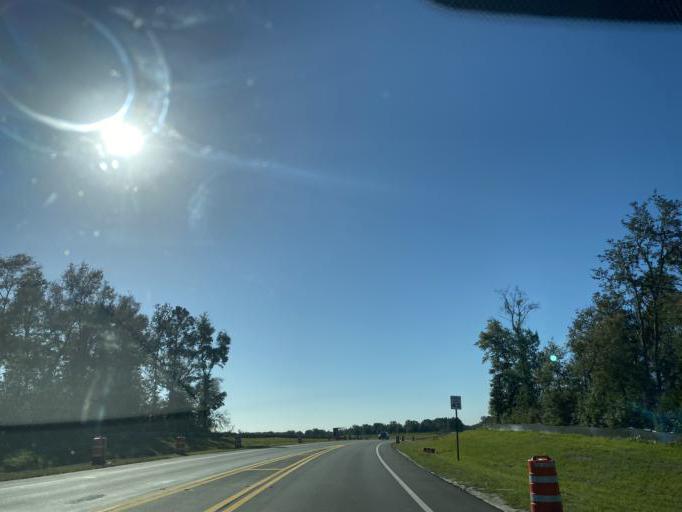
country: US
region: Florida
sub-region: Lake County
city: Mount Plymouth
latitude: 28.8291
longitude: -81.5213
